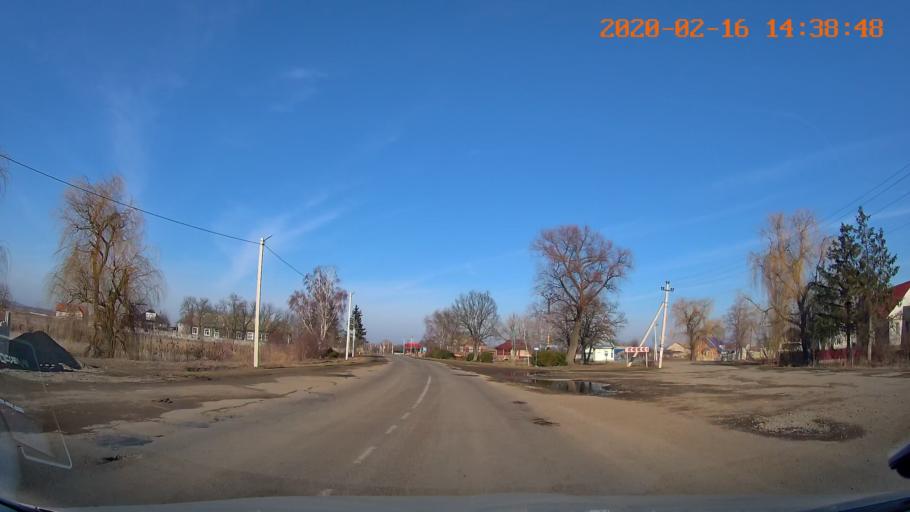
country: RO
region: Botosani
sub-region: Comuna Darabani
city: Bajura
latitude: 48.2350
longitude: 26.5459
